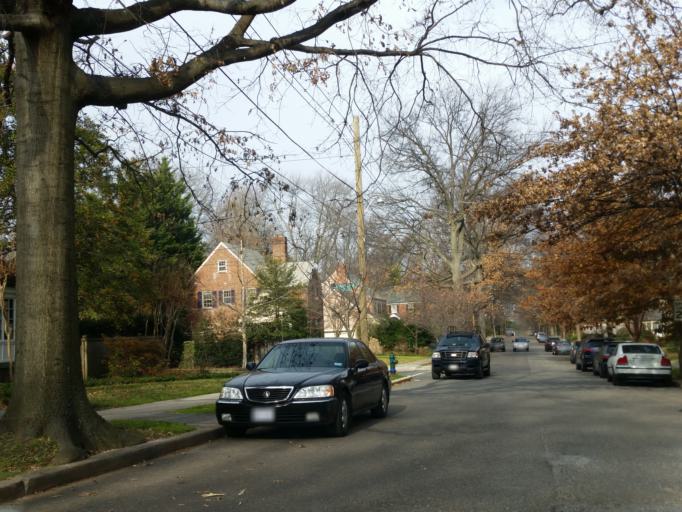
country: US
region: Maryland
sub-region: Montgomery County
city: Chevy Chase
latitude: 38.9702
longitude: -77.0663
